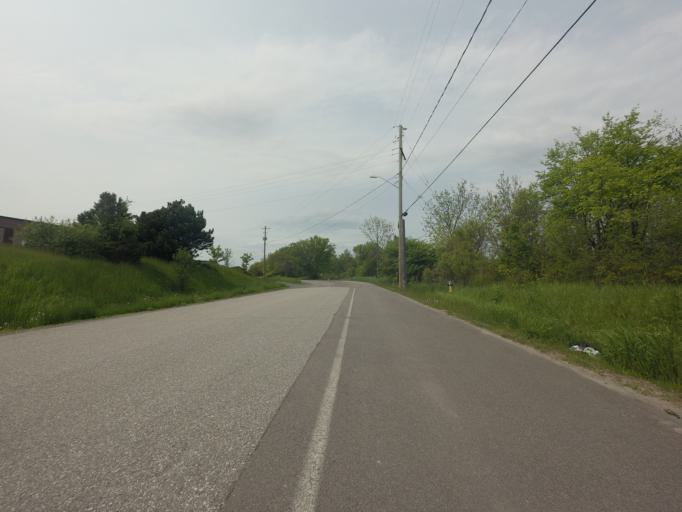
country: CA
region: Ontario
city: Kingston
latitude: 44.2538
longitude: -76.4901
